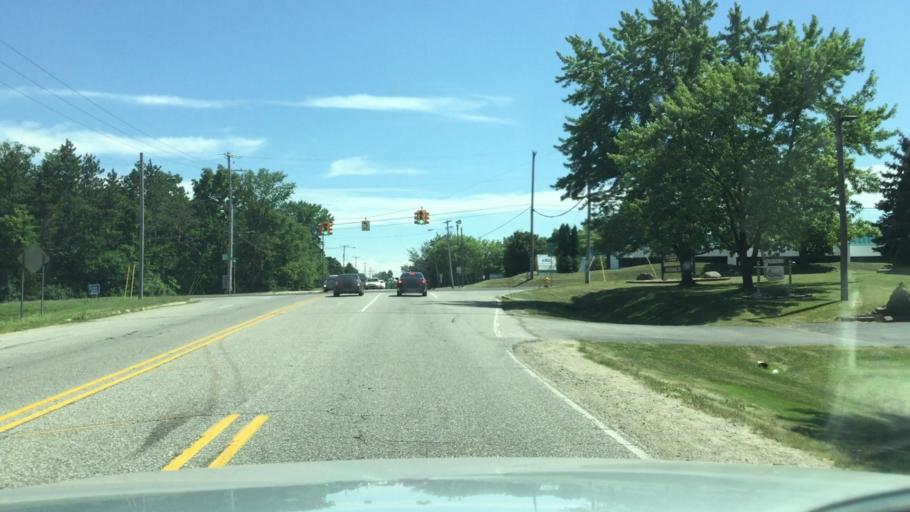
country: US
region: Michigan
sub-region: Genesee County
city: Flint
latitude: 43.0076
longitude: -83.7531
